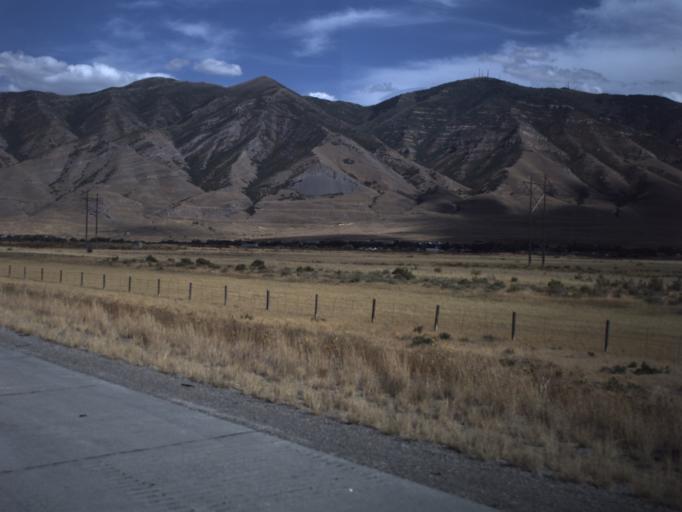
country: US
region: Utah
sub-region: Tooele County
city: Stansbury park
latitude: 40.6740
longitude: -112.2891
